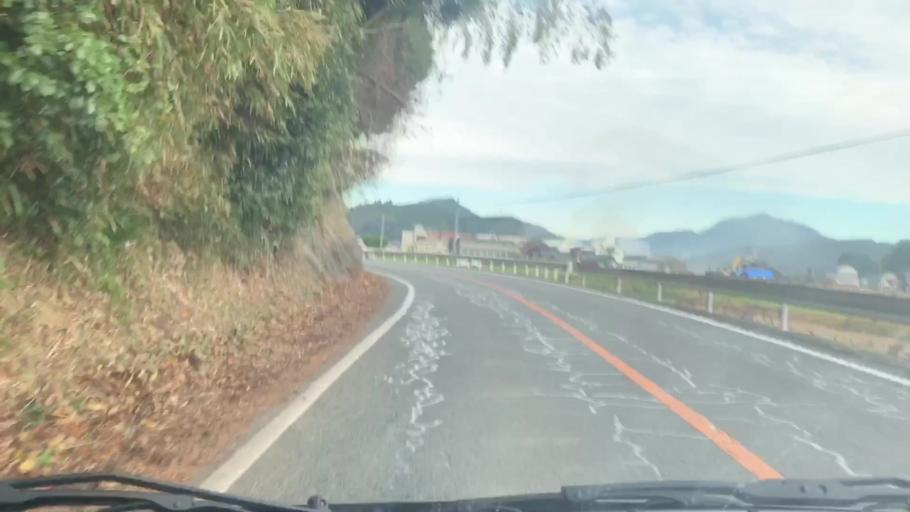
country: JP
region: Saga Prefecture
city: Takeocho-takeo
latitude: 33.2244
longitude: 129.9644
